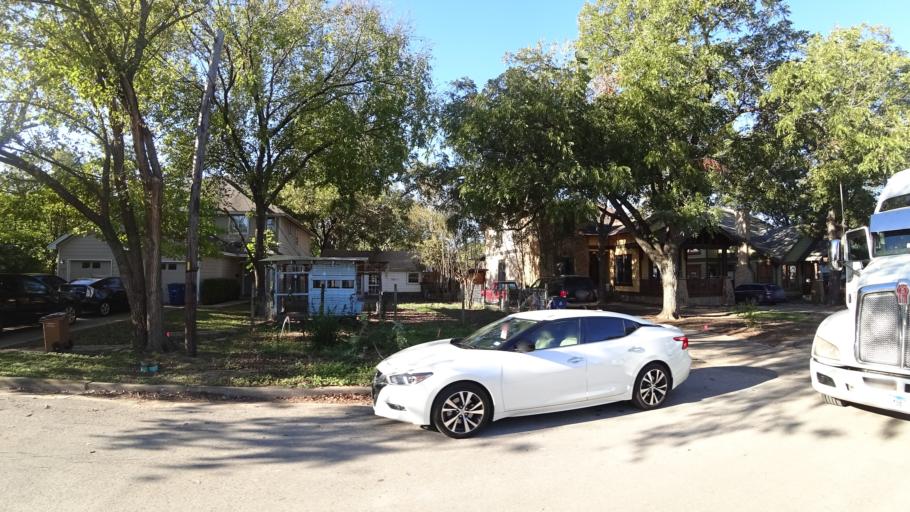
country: US
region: Texas
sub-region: Travis County
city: Austin
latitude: 30.3112
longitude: -97.7193
